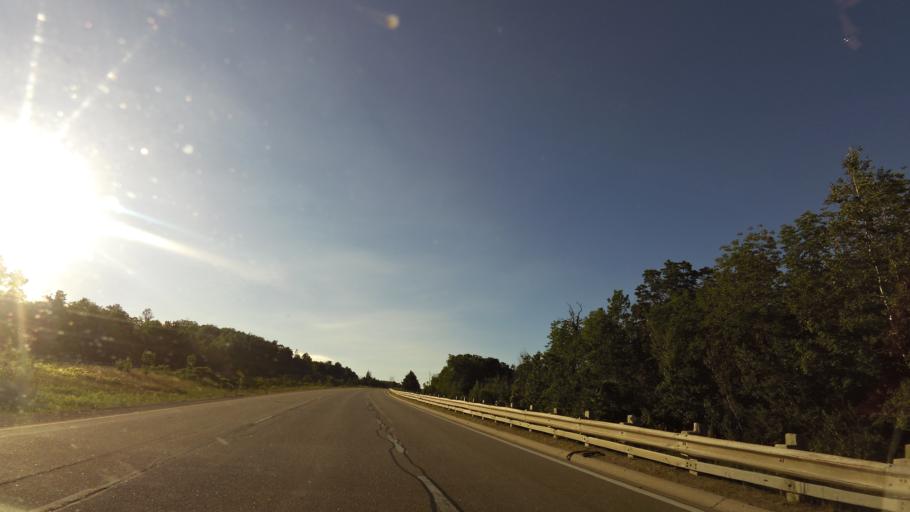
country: CA
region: Ontario
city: Midland
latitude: 44.7074
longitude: -79.6625
